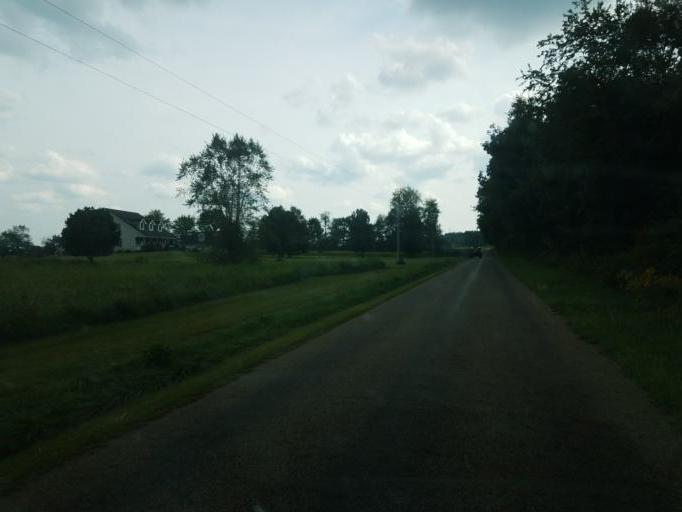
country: US
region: Ohio
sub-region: Knox County
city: Gambier
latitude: 40.3473
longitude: -82.3484
